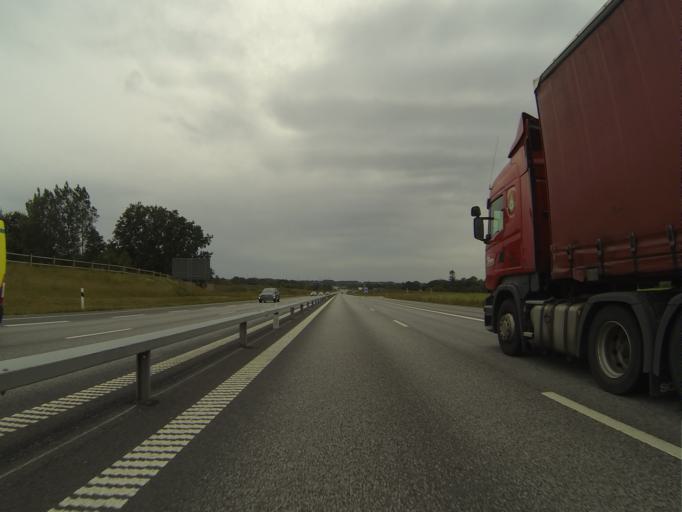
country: SE
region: Skane
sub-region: Hoors Kommun
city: Loberod
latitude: 55.8106
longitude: 13.4832
